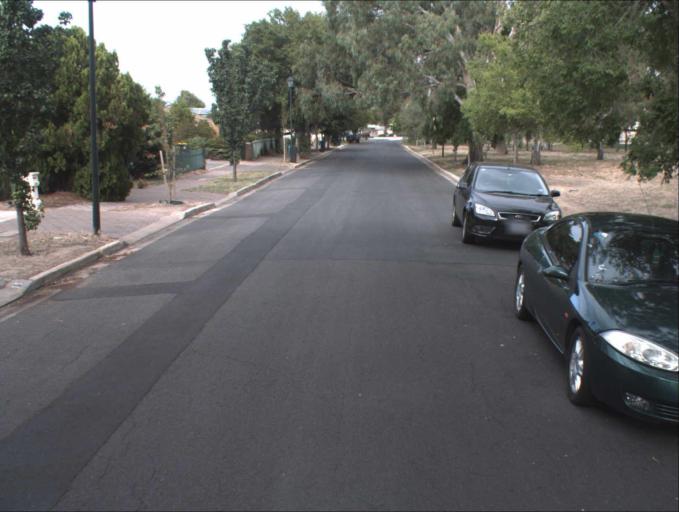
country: AU
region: South Australia
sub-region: Port Adelaide Enfield
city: Gilles Plains
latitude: -34.8627
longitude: 138.6404
